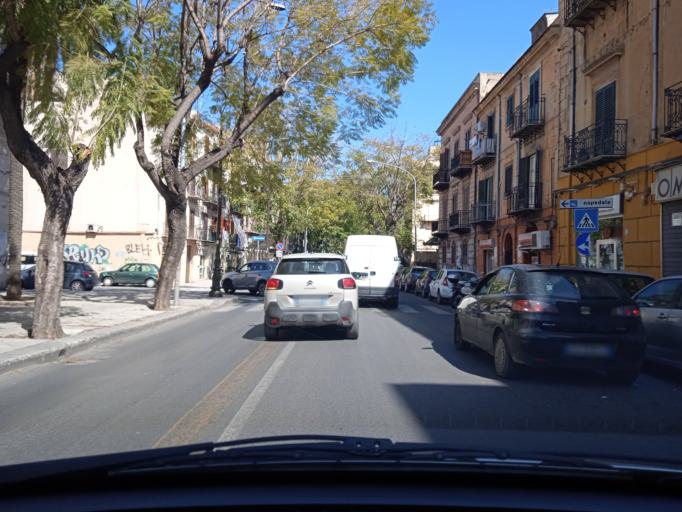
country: IT
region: Sicily
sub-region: Palermo
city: Palermo
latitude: 38.1085
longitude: 13.3577
